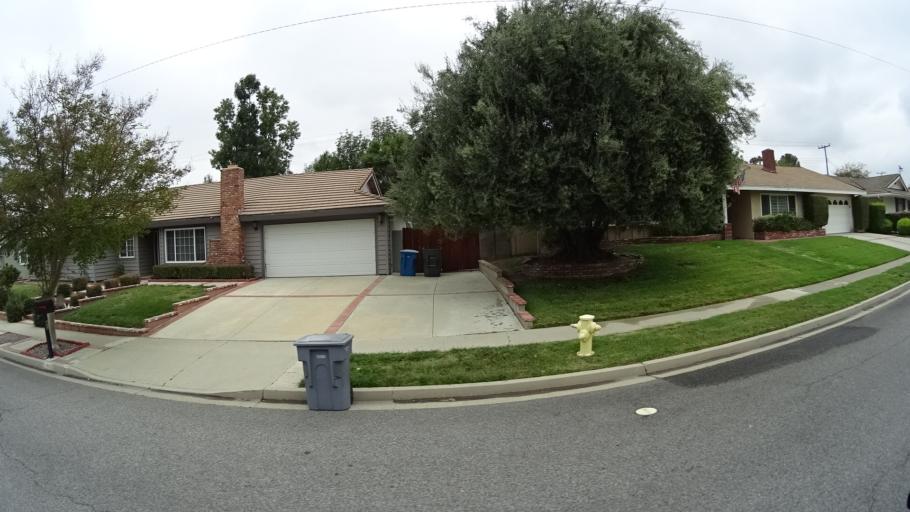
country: US
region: California
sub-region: Ventura County
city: Thousand Oaks
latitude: 34.2064
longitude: -118.8758
